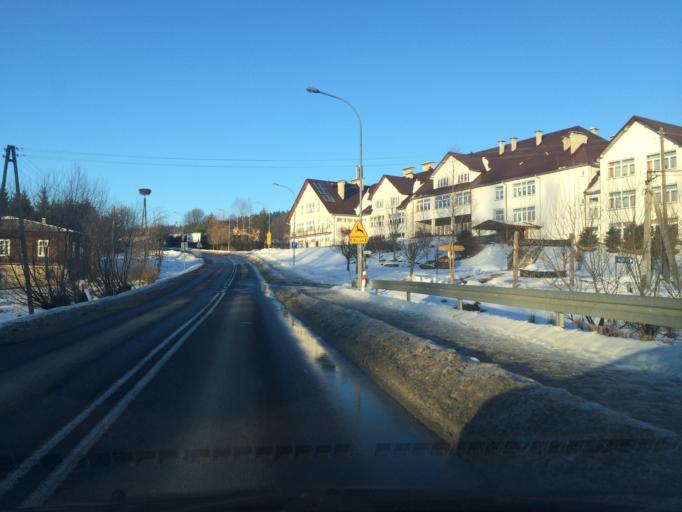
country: PL
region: Subcarpathian Voivodeship
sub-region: Powiat bieszczadzki
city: Lutowiska
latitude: 49.2493
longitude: 22.6955
